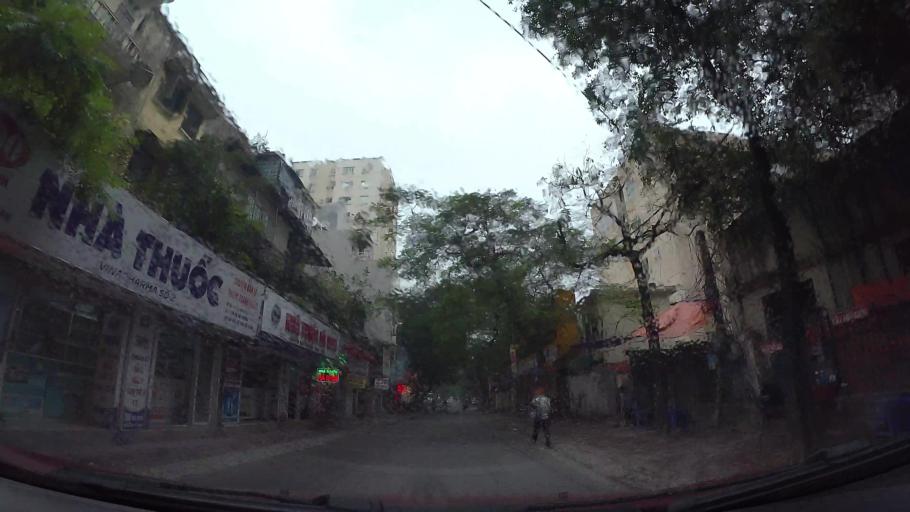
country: VN
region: Ha Noi
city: Dong Da
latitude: 21.0143
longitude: 105.8145
